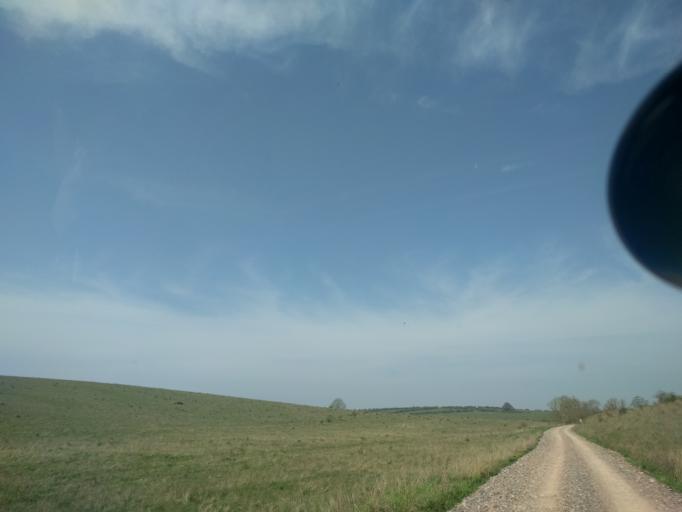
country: GB
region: England
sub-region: Wiltshire
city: Edington
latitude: 51.2423
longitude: -2.0974
